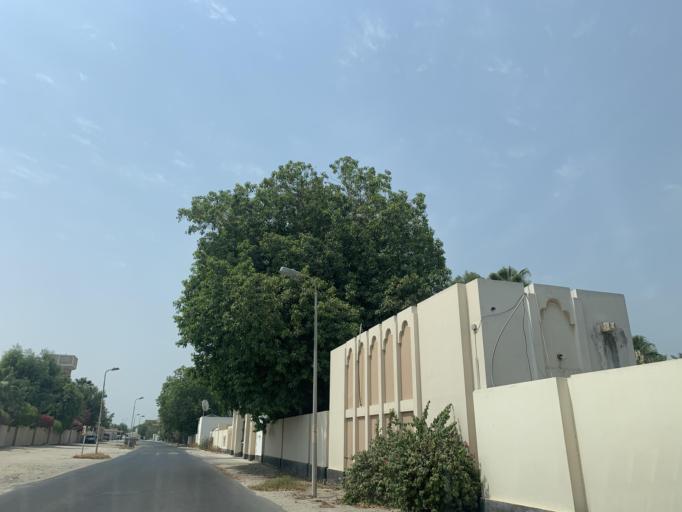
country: BH
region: Manama
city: Jidd Hafs
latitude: 26.2038
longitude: 50.4866
